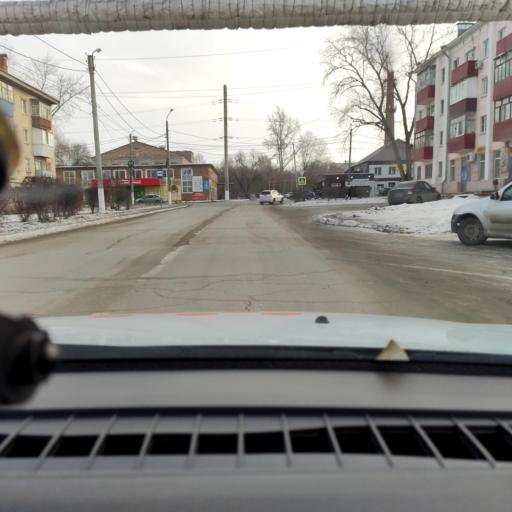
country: RU
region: Samara
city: Chapayevsk
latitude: 52.9720
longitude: 49.7051
